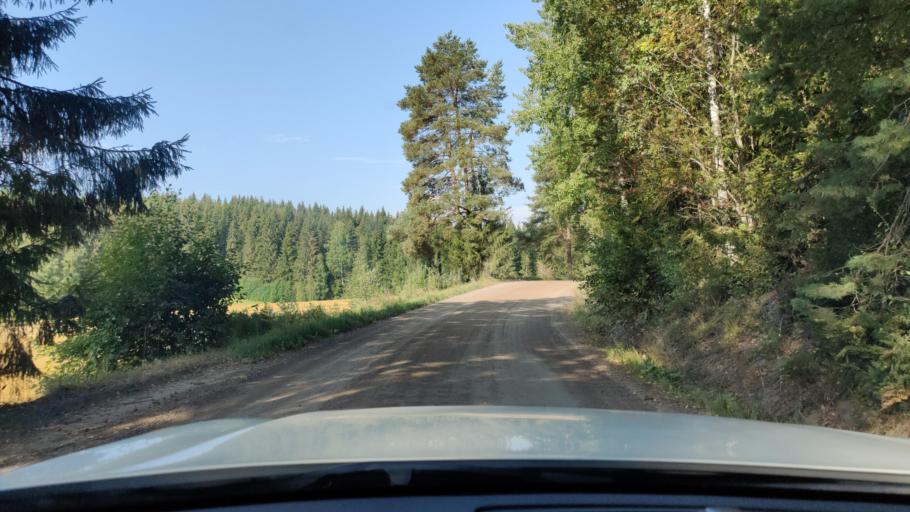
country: FI
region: Haeme
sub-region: Haemeenlinna
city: Tervakoski
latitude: 60.6751
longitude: 24.6013
